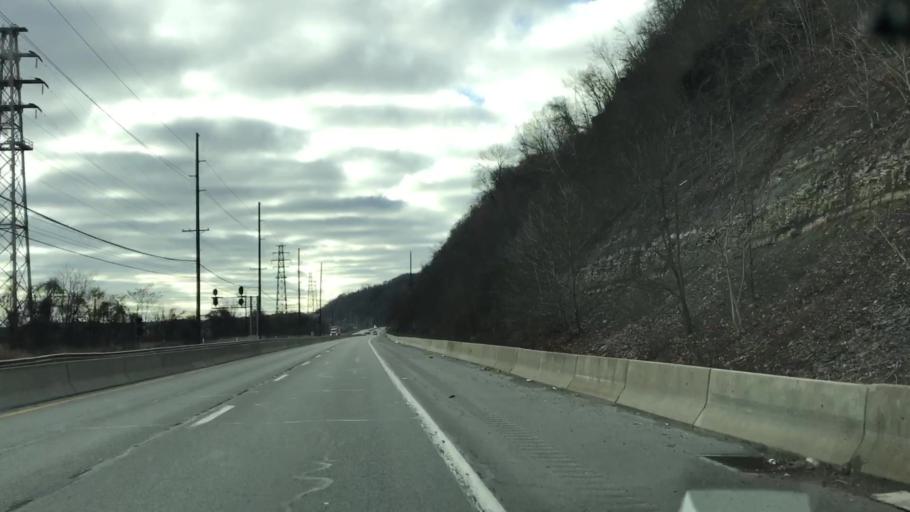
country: US
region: Pennsylvania
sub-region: Beaver County
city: Economy
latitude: 40.6101
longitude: -80.2424
